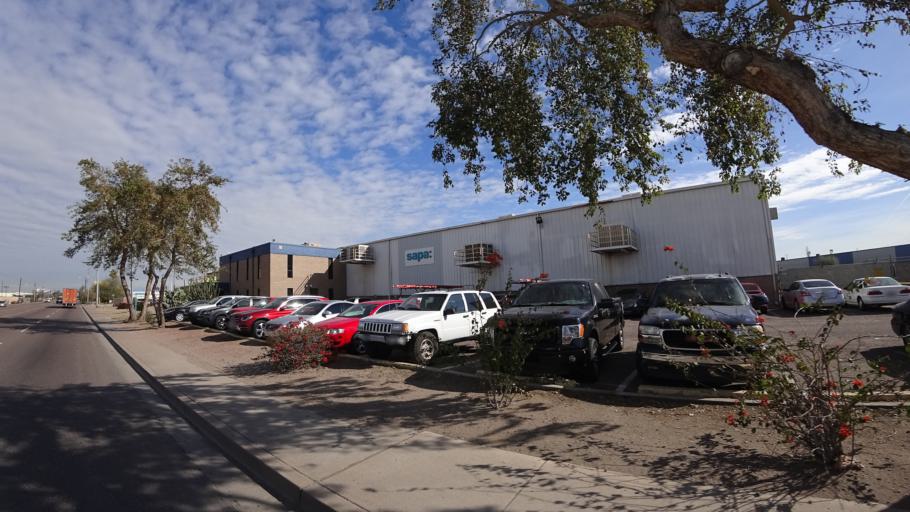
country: US
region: Arizona
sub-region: Maricopa County
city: Laveen
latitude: 33.4452
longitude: -112.1691
